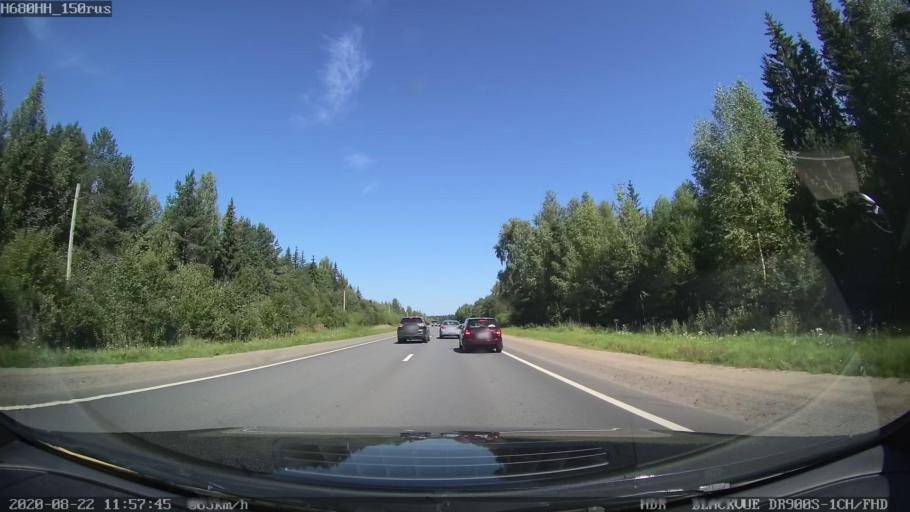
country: RU
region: Tverskaya
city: Rameshki
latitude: 57.1841
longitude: 36.0819
